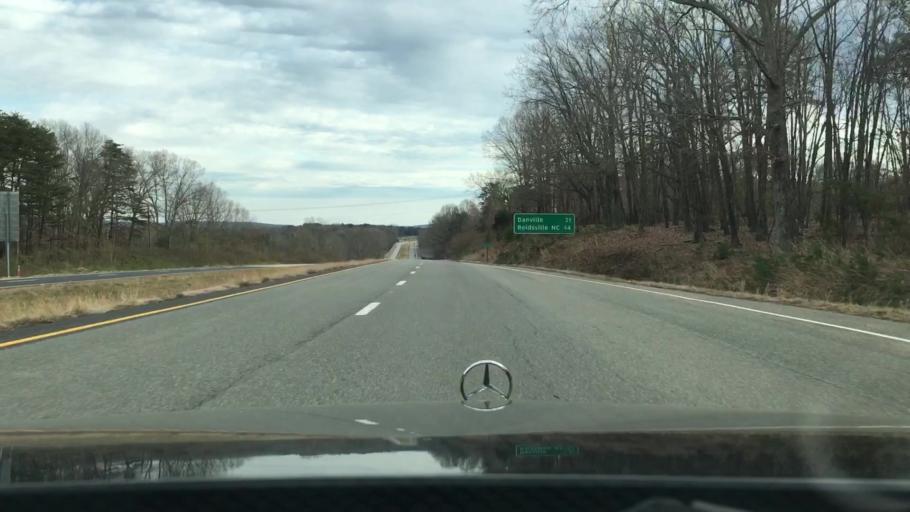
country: US
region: Virginia
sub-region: Pittsylvania County
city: Chatham
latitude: 36.8461
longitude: -79.3919
